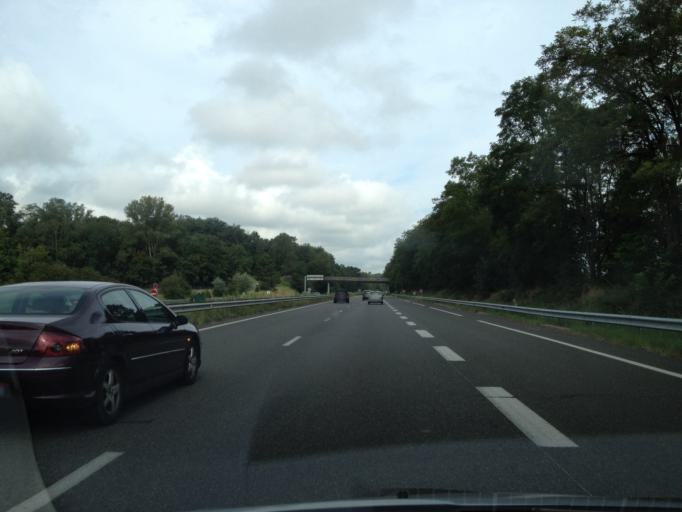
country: FR
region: Aquitaine
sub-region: Departement du Lot-et-Garonne
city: Layrac
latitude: 44.1267
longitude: 0.6944
